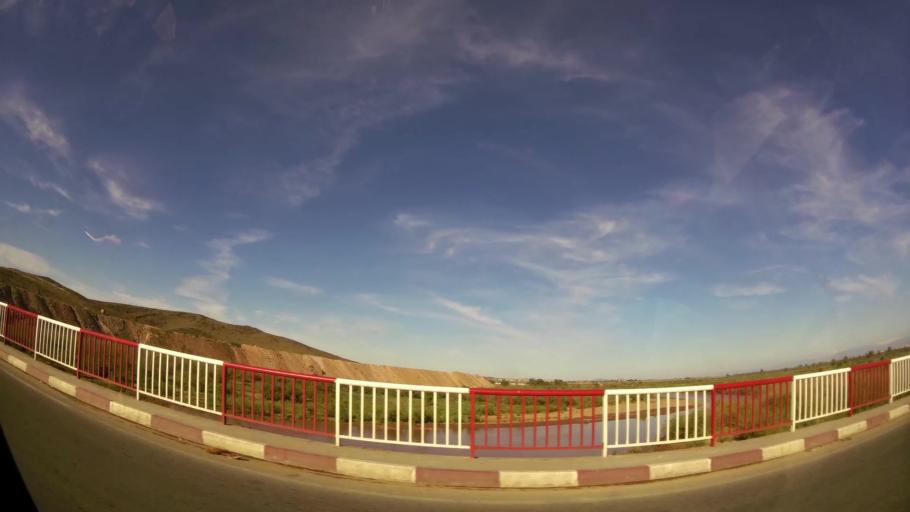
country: MA
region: Marrakech-Tensift-Al Haouz
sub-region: Marrakech
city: Marrakesh
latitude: 31.7008
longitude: -8.0609
